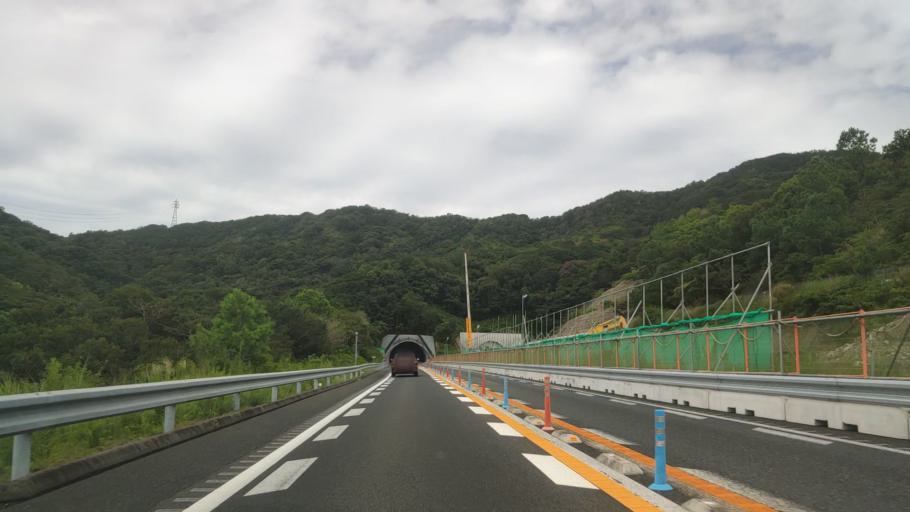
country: JP
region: Wakayama
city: Gobo
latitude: 33.8475
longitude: 135.2173
